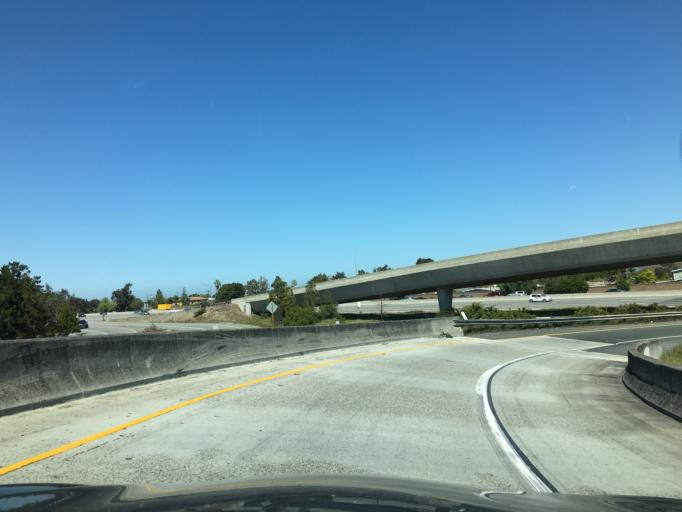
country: US
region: California
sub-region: San Mateo County
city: Foster City
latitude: 37.5537
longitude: -122.2981
